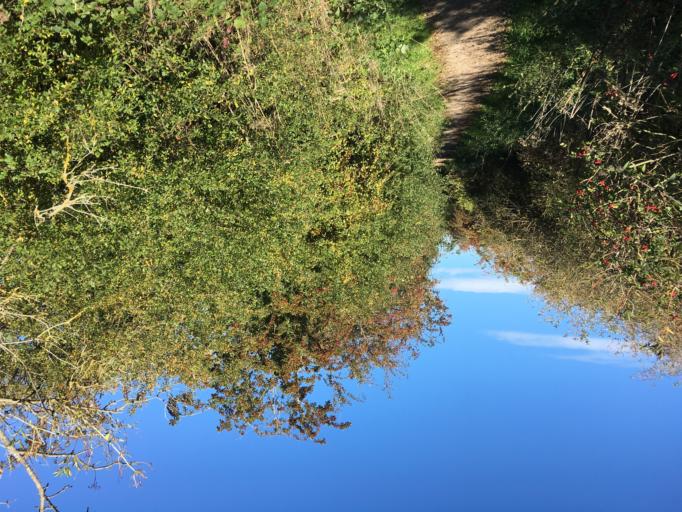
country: GB
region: England
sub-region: Solihull
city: Balsall Common
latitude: 52.3901
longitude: -1.6272
